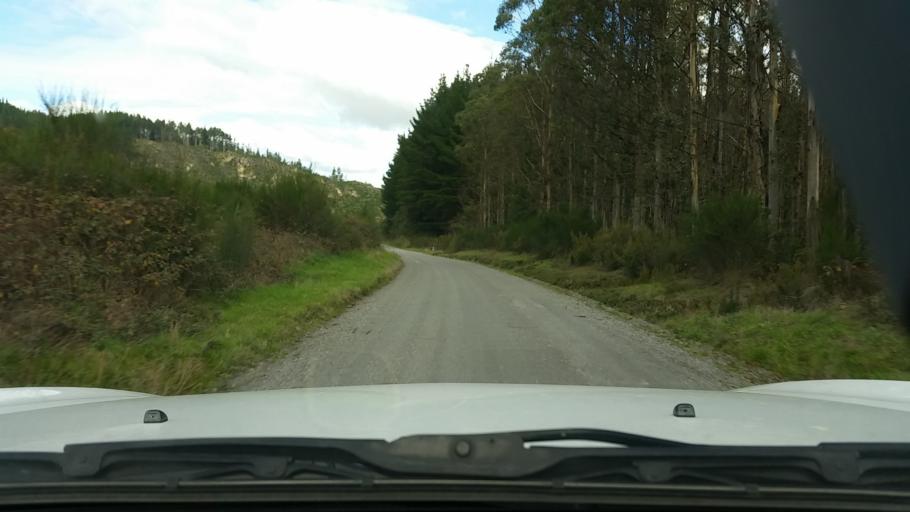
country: NZ
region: Waikato
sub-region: Taupo District
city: Taupo
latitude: -38.4617
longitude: 176.1595
